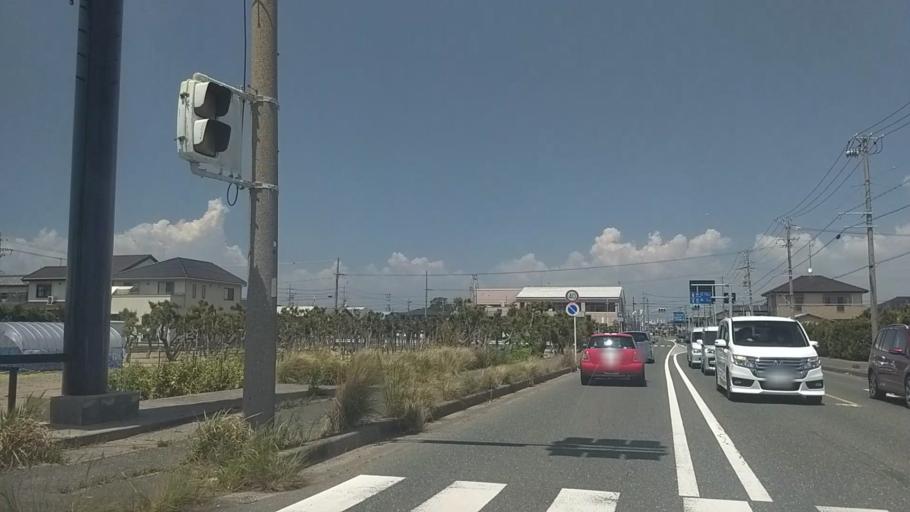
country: JP
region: Shizuoka
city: Hamamatsu
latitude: 34.6807
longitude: 137.6305
